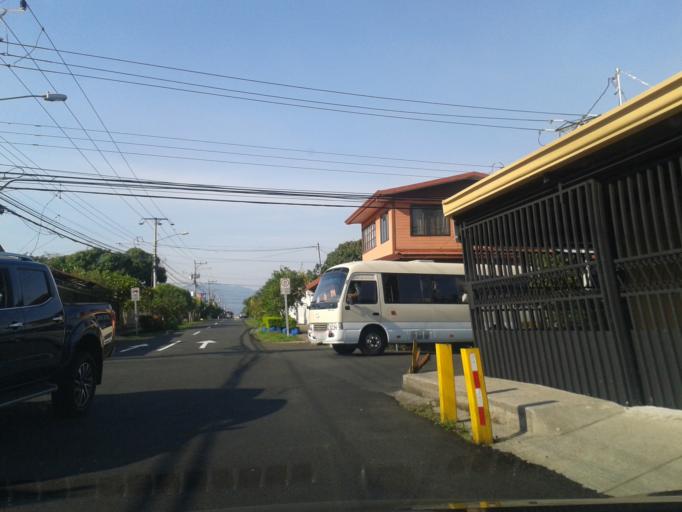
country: CR
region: Heredia
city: Llorente
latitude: 10.0059
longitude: -84.1524
